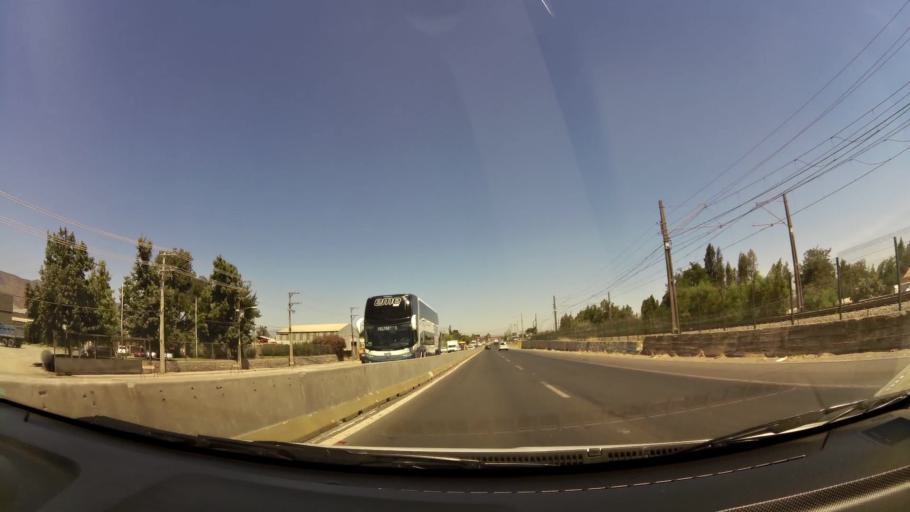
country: CL
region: O'Higgins
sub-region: Provincia de Cachapoal
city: Rancagua
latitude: -34.1965
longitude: -70.7573
